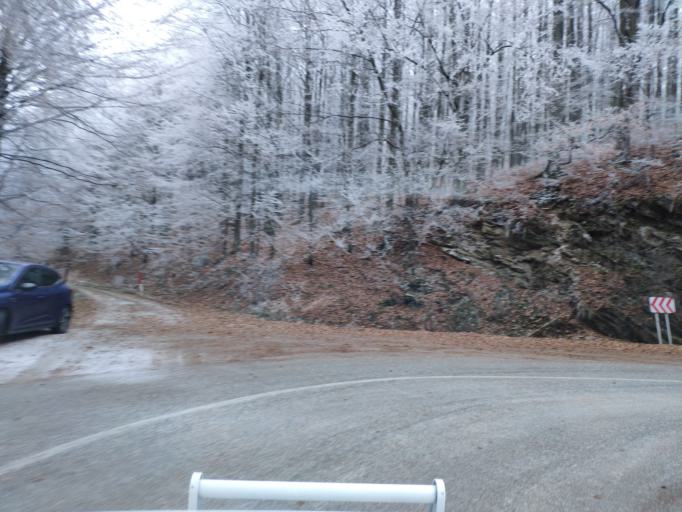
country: SK
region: Kosicky
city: Dobsina
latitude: 48.7999
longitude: 20.4813
